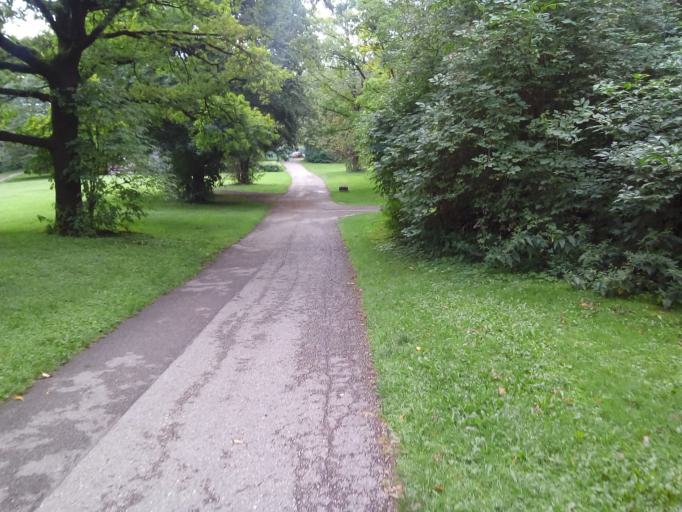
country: DE
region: Bavaria
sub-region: Upper Bavaria
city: Unterfoehring
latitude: 48.1917
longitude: 11.6668
